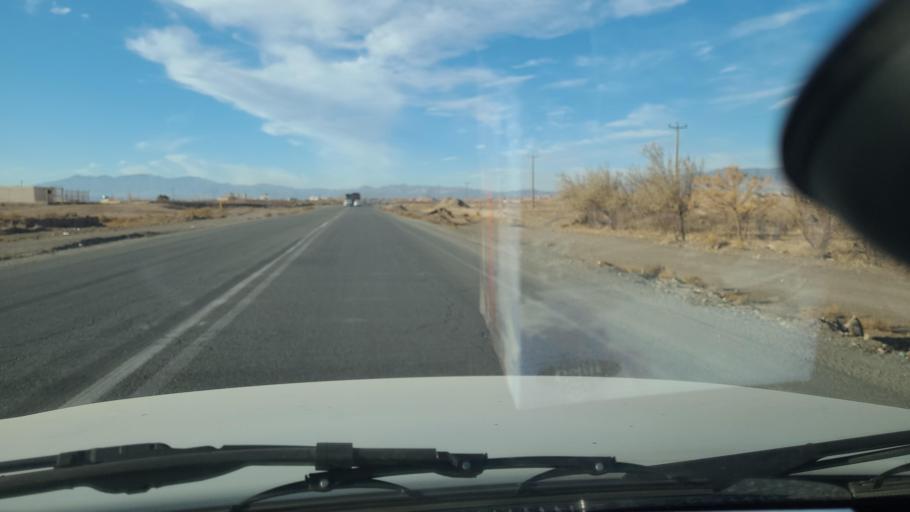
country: IR
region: Razavi Khorasan
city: Sabzevar
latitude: 36.2360
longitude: 57.6435
